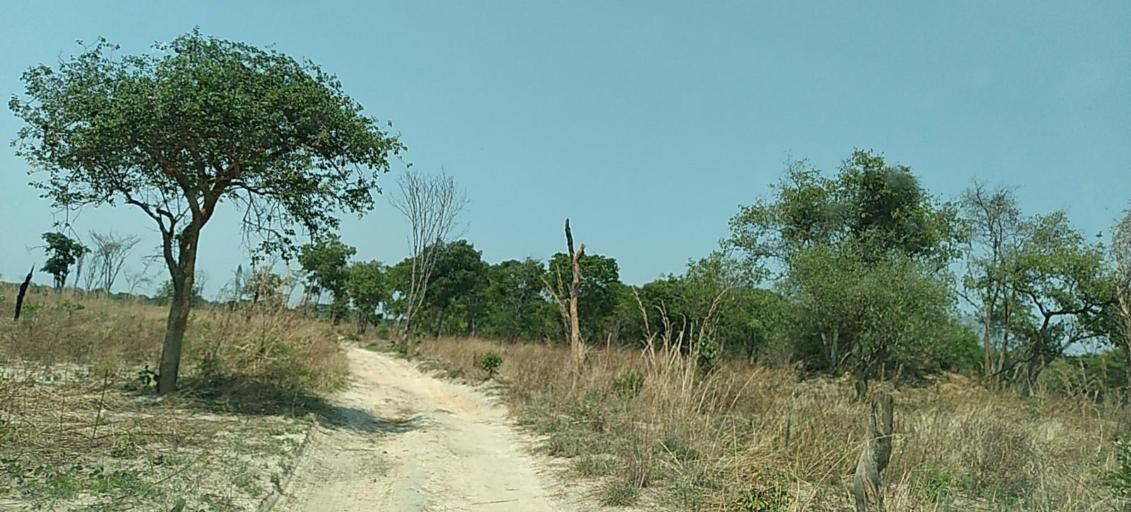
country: ZM
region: Copperbelt
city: Mpongwe
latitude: -13.8707
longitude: 28.0489
